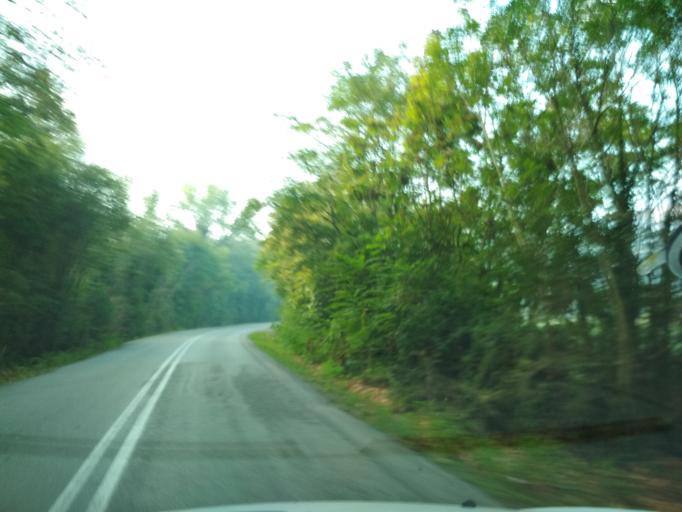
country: GR
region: Central Greece
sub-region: Nomos Evvoias
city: Prokopion
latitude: 38.7449
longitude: 23.4889
